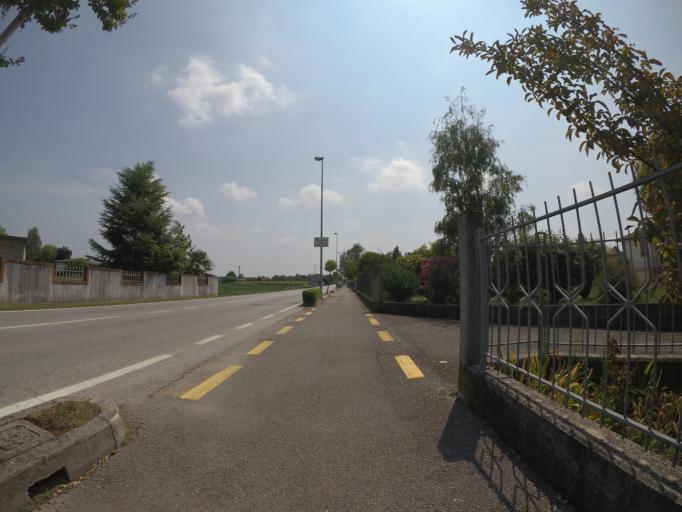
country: IT
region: Friuli Venezia Giulia
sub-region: Provincia di Udine
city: Teor
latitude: 45.8603
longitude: 13.0524
